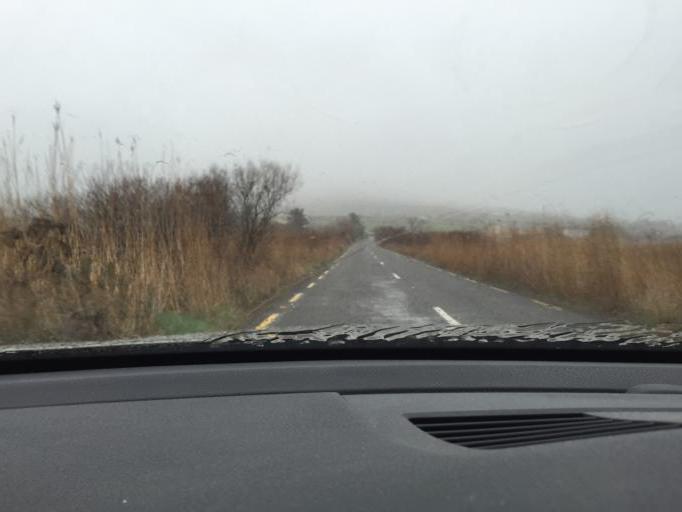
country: IE
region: Munster
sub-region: Ciarrai
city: Dingle
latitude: 52.1342
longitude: -10.3702
